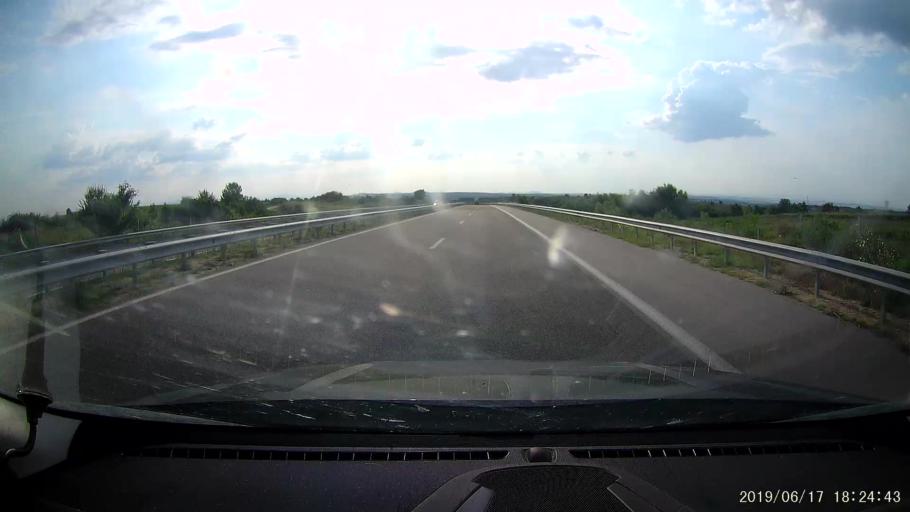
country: BG
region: Khaskovo
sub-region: Obshtina Dimitrovgrad
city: Dimitrovgrad
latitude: 41.9871
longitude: 25.6833
